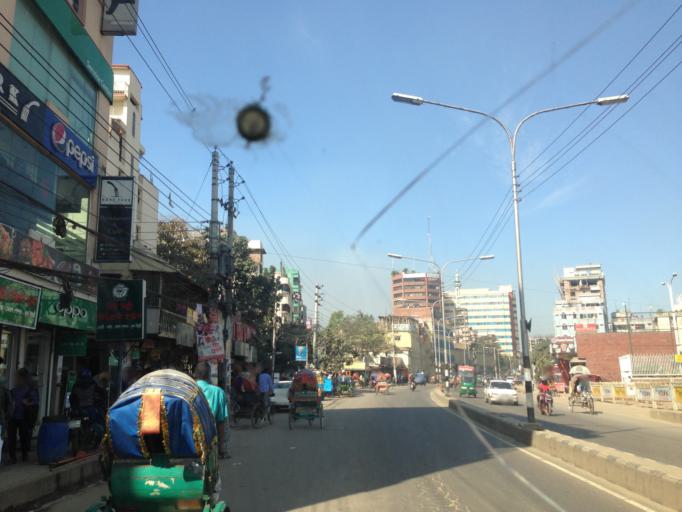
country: BD
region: Dhaka
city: Azimpur
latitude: 23.8072
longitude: 90.3619
